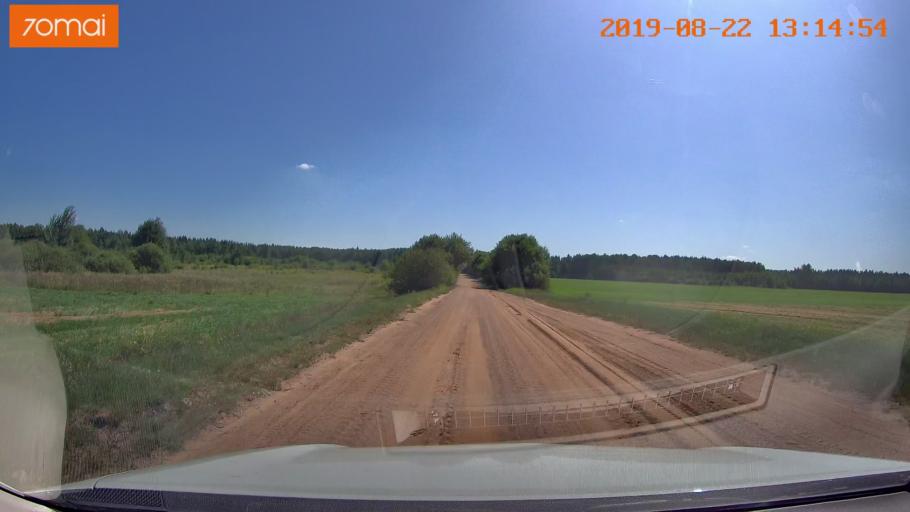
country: BY
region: Minsk
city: Prawdzinski
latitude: 53.2643
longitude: 27.8914
